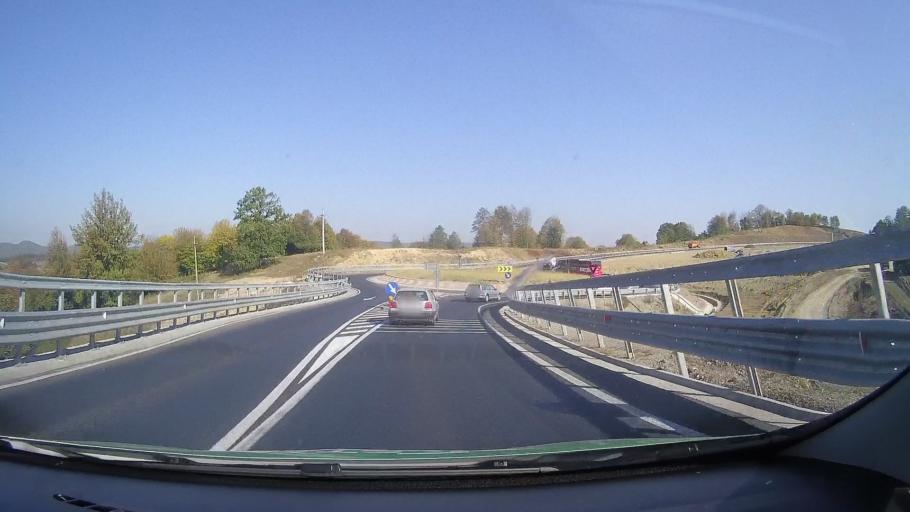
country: RO
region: Timis
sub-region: Comuna Pietroasa
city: Pietroasa
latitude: 45.8855
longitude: 22.4030
